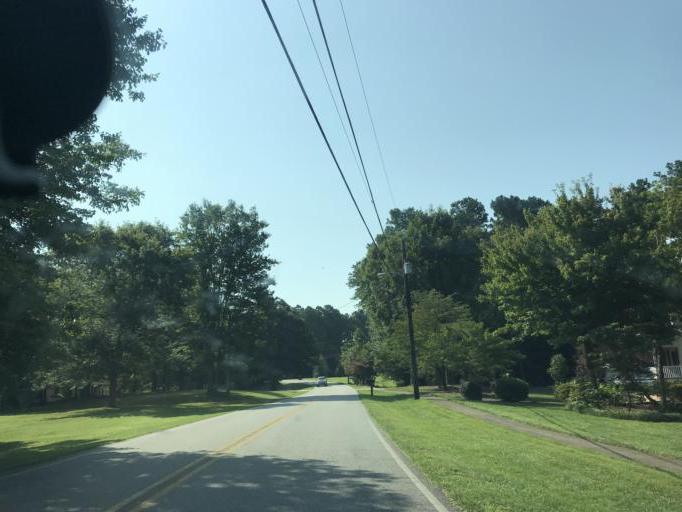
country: US
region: Georgia
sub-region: Forsyth County
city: Cumming
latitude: 34.2311
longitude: -84.1223
